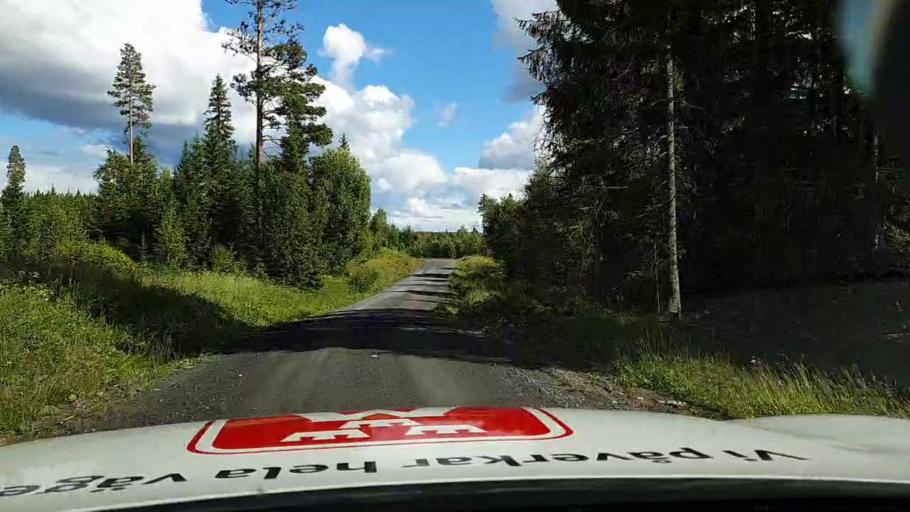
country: SE
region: Jaemtland
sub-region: Krokoms Kommun
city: Valla
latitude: 63.3274
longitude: 13.7360
